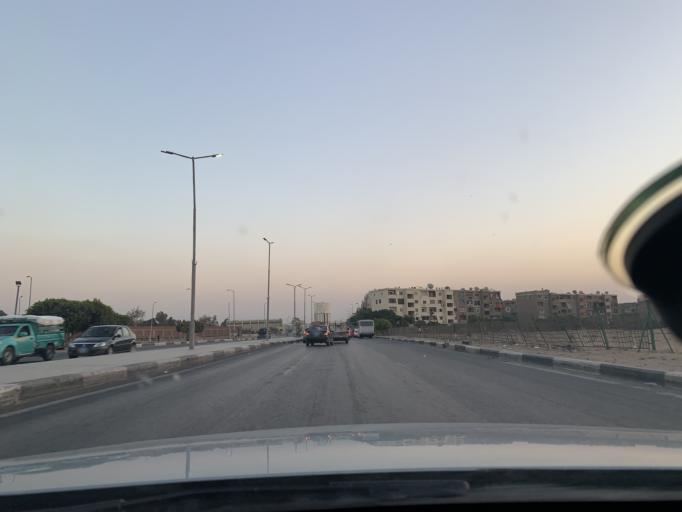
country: EG
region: Muhafazat al Qalyubiyah
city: Al Khankah
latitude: 30.1720
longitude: 31.4259
